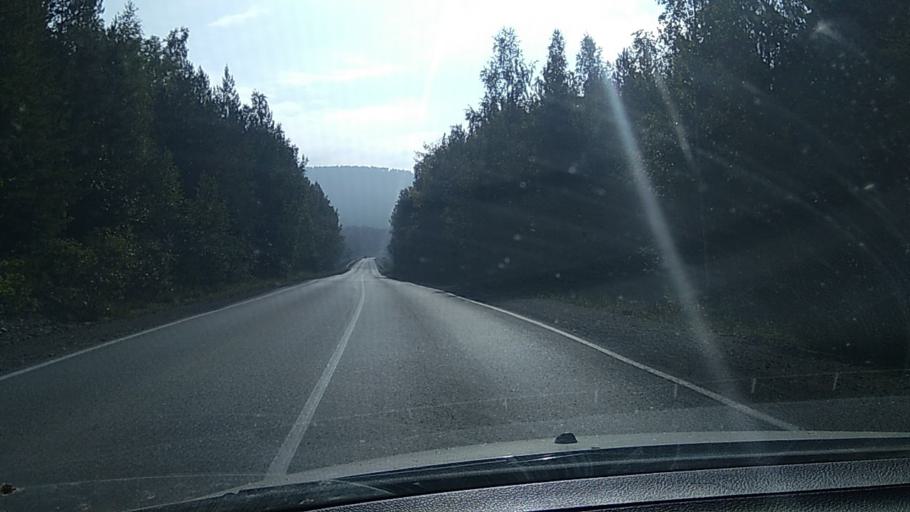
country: RU
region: Chelyabinsk
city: Karabash
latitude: 55.4244
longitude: 60.2641
